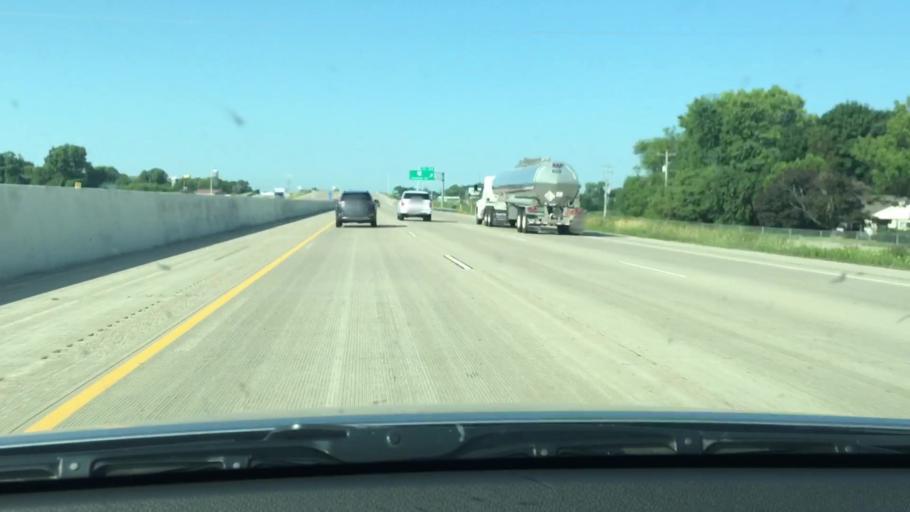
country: US
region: Wisconsin
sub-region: Winnebago County
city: Oshkosh
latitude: 44.1017
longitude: -88.5369
